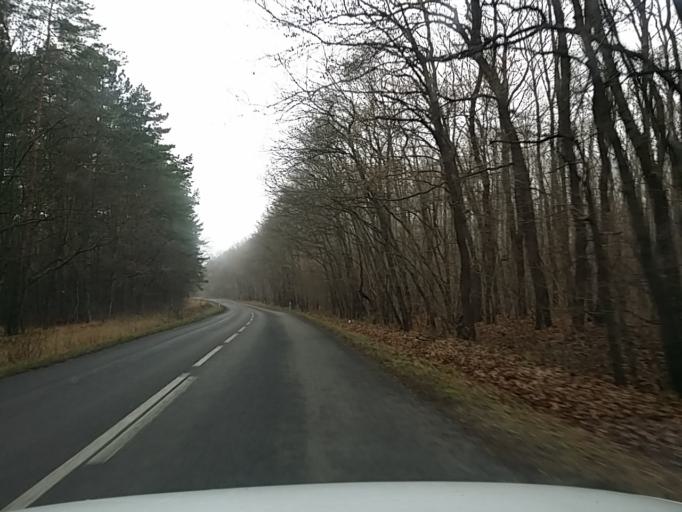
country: HU
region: Pest
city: Paty
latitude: 47.5313
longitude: 18.8651
